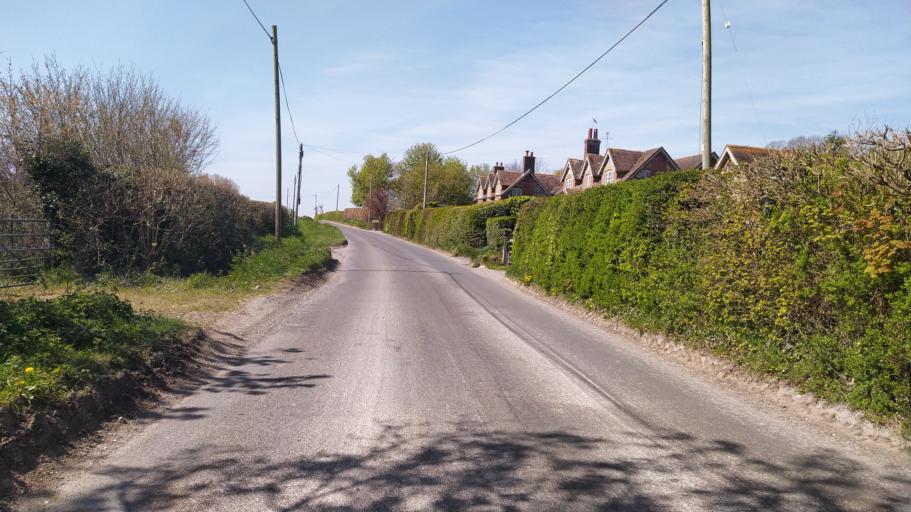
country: GB
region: England
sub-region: Dorset
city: Manston
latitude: 50.9044
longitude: -2.2238
